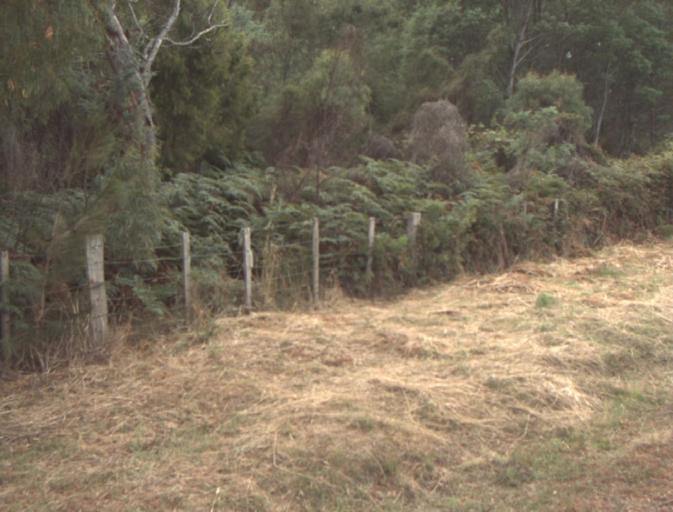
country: AU
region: Tasmania
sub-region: Launceston
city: Mayfield
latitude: -41.2830
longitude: 147.0405
